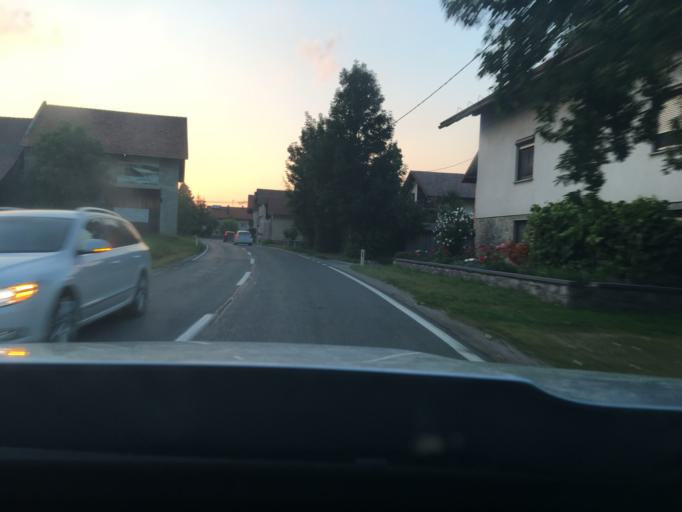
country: SI
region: Ribnica
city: Ribnica
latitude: 45.7195
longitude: 14.7450
